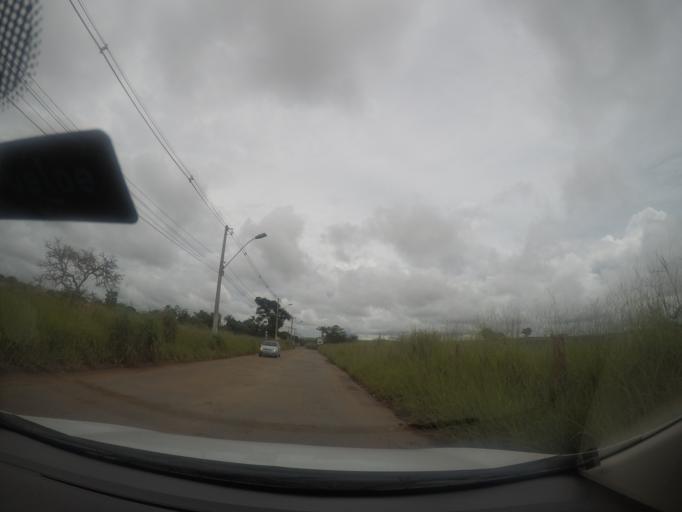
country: BR
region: Goias
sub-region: Trindade
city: Trindade
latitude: -16.6835
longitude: -49.4020
